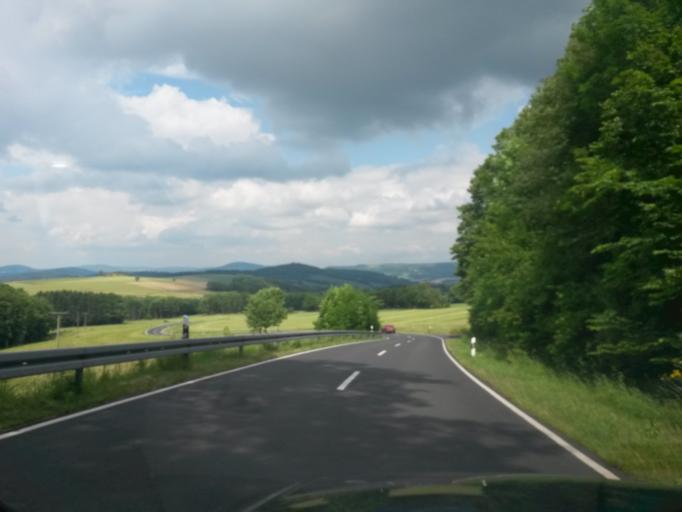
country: DE
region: Hesse
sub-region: Regierungsbezirk Kassel
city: Gersfeld
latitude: 50.5132
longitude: 9.9303
